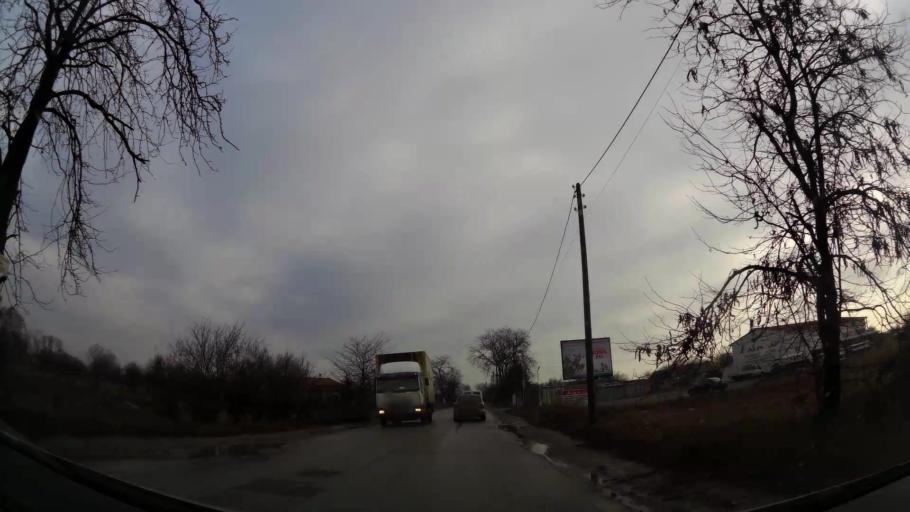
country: BG
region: Sofia-Capital
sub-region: Stolichna Obshtina
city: Sofia
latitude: 42.7231
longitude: 23.3686
